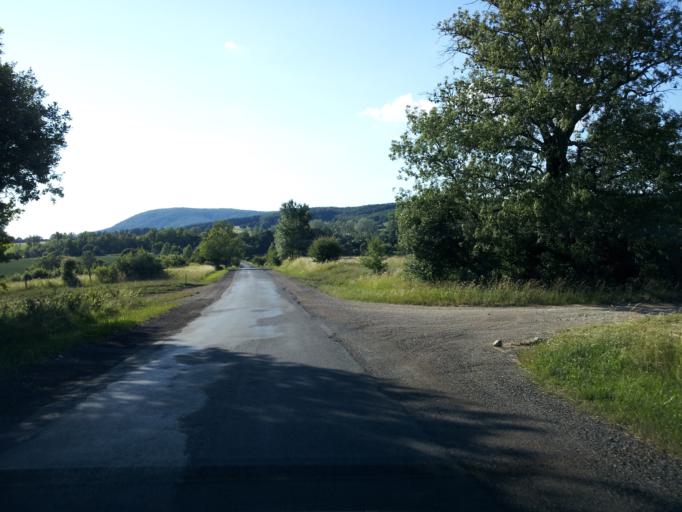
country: HU
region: Veszprem
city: Zirc
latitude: 47.2236
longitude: 17.8320
